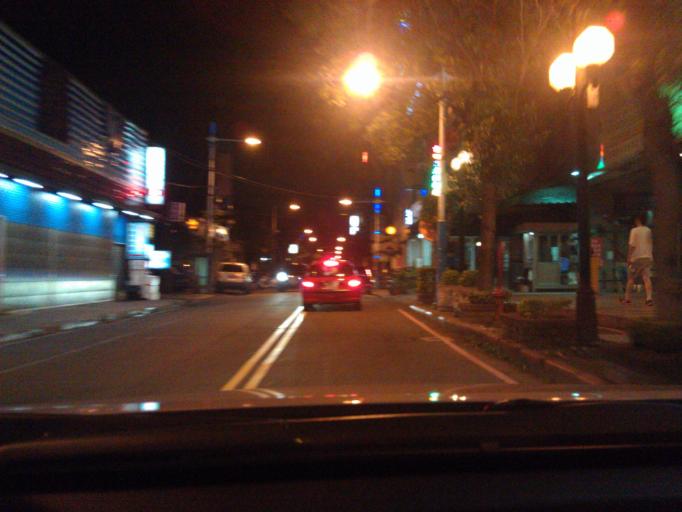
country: TW
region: Taipei
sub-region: Taipei
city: Banqiao
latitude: 25.0263
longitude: 121.4701
